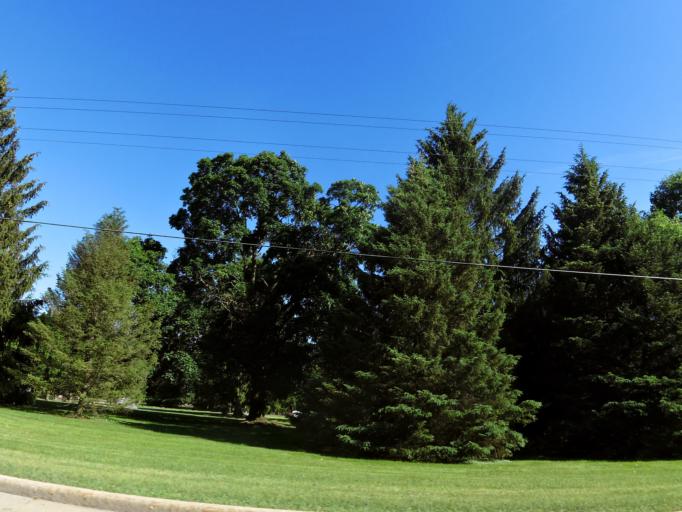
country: US
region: Wisconsin
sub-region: Rock County
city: Beloit
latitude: 42.5177
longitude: -89.0002
